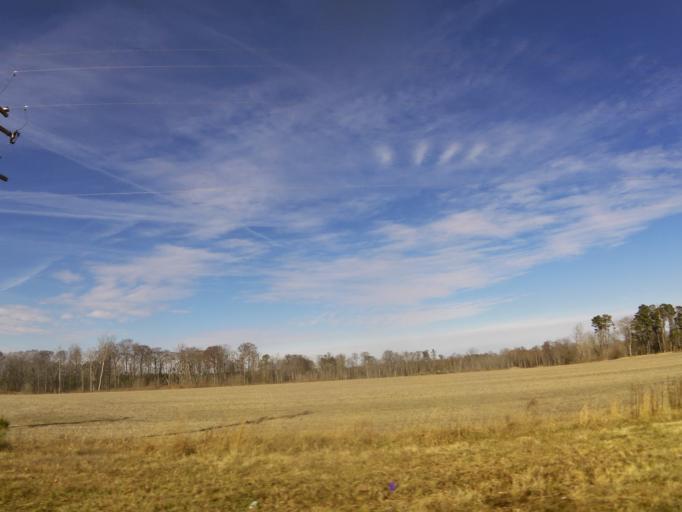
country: US
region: Virginia
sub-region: Isle of Wight County
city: Windsor
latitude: 36.7822
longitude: -76.8230
